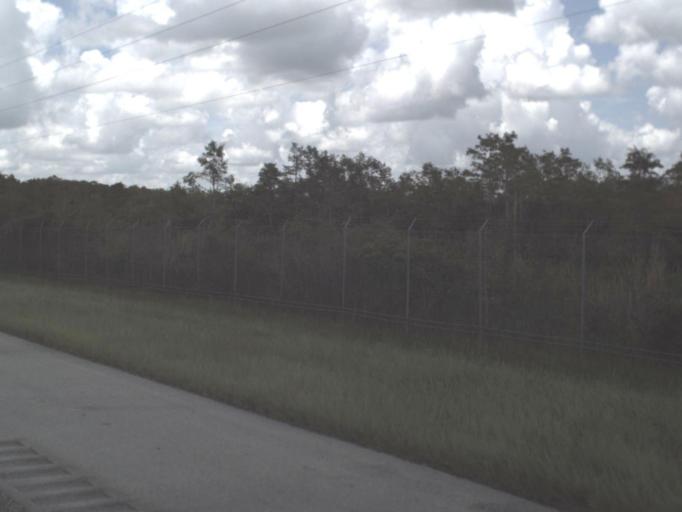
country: US
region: Florida
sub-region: Broward County
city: Weston
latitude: 26.1718
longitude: -80.9322
